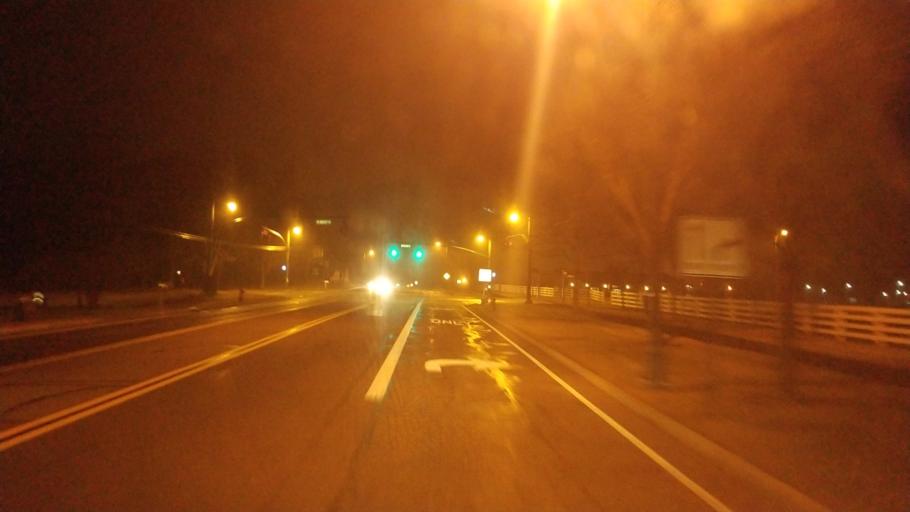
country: US
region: Ohio
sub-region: Franklin County
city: New Albany
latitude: 40.0922
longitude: -82.7893
